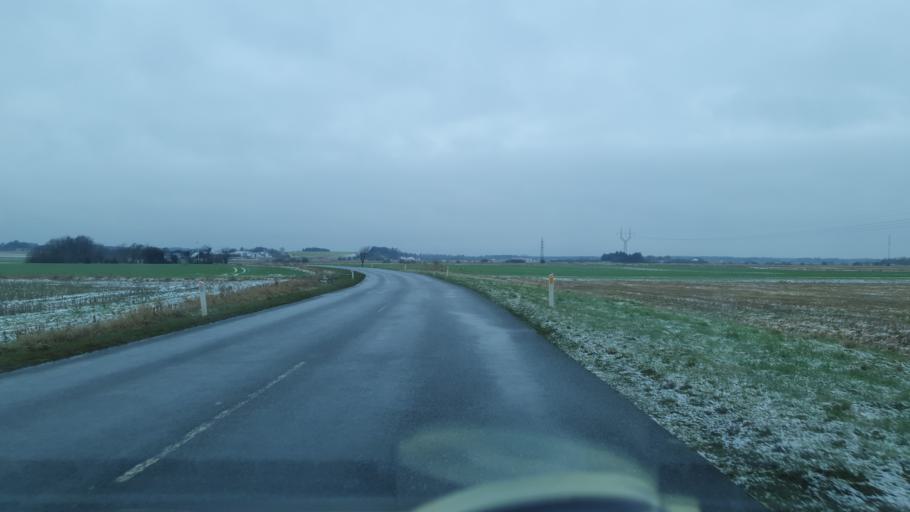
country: DK
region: North Denmark
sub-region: Jammerbugt Kommune
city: Brovst
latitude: 57.1153
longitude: 9.5005
